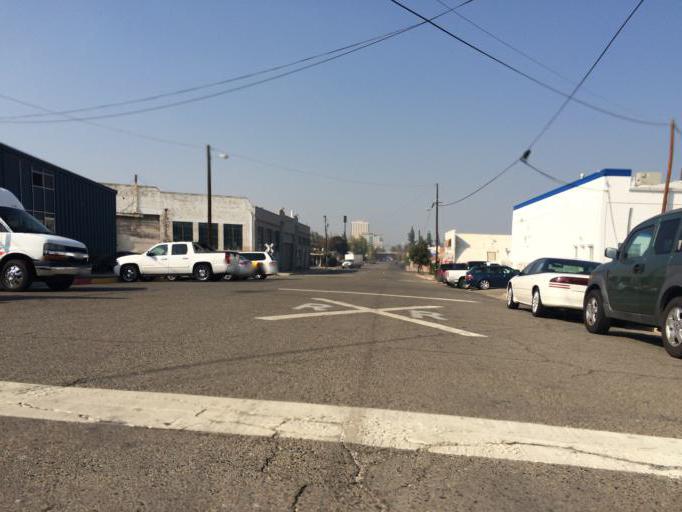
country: US
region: California
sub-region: Fresno County
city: Fresno
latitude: 36.7273
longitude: -119.7773
